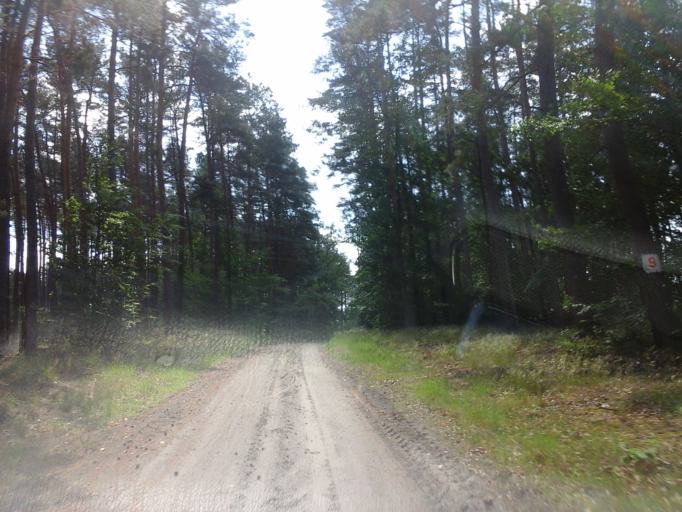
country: PL
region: West Pomeranian Voivodeship
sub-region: Powiat choszczenski
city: Bierzwnik
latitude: 53.0836
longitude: 15.7206
